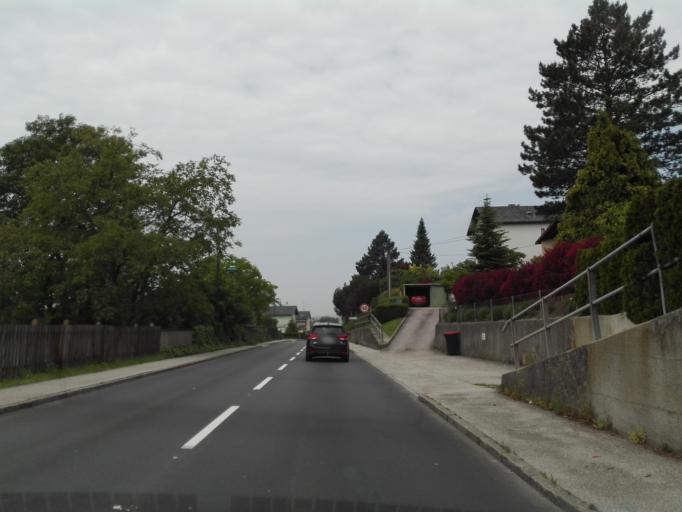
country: AT
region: Upper Austria
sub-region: Politischer Bezirk Urfahr-Umgebung
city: Ottensheim
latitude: 48.2830
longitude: 14.1523
